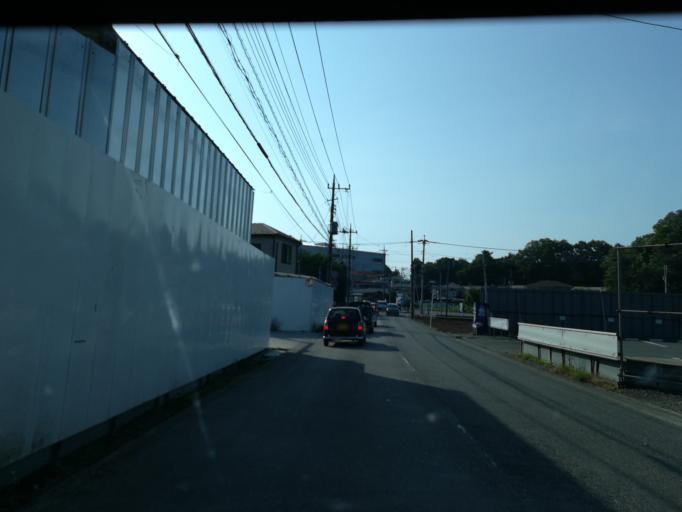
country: JP
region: Saitama
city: Sayama
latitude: 35.8050
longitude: 139.3811
